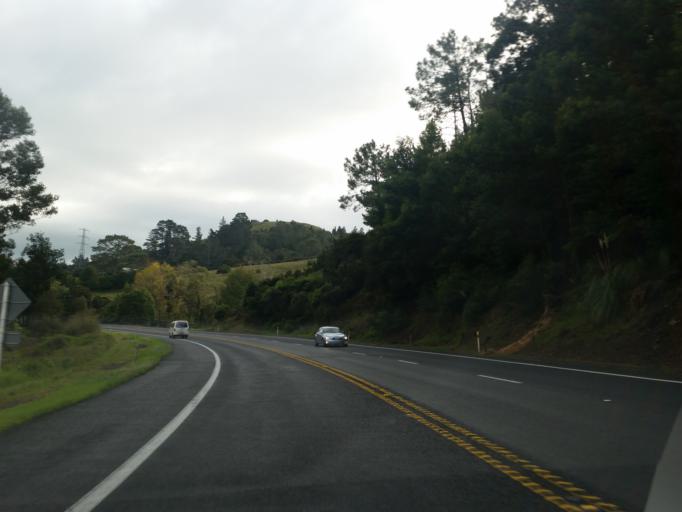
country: NZ
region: Waikato
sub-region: Hauraki District
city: Paeroa
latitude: -37.4041
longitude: 175.7081
